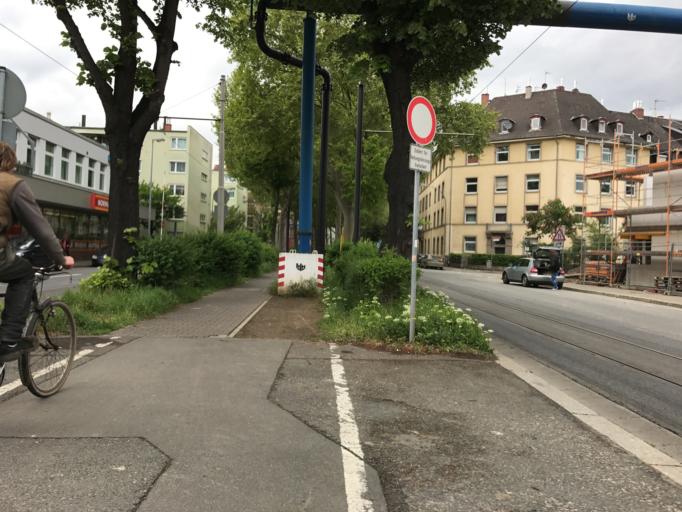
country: DE
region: Rheinland-Pfalz
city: Mainz
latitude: 50.0103
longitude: 8.2505
